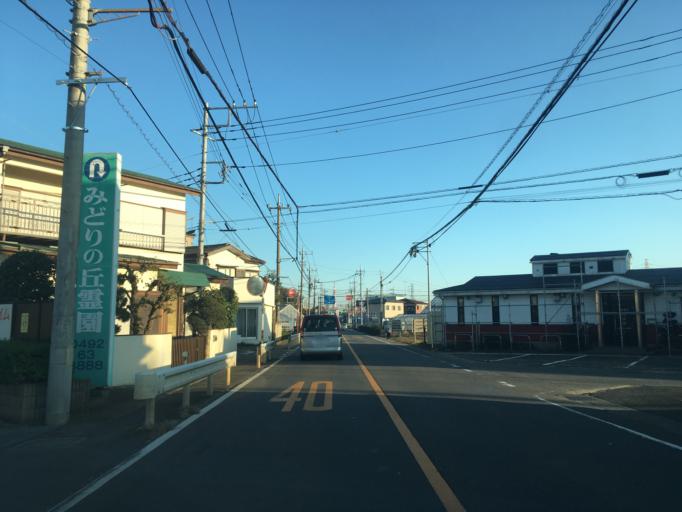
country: JP
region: Saitama
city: Kawagoe
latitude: 35.8853
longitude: 139.4766
